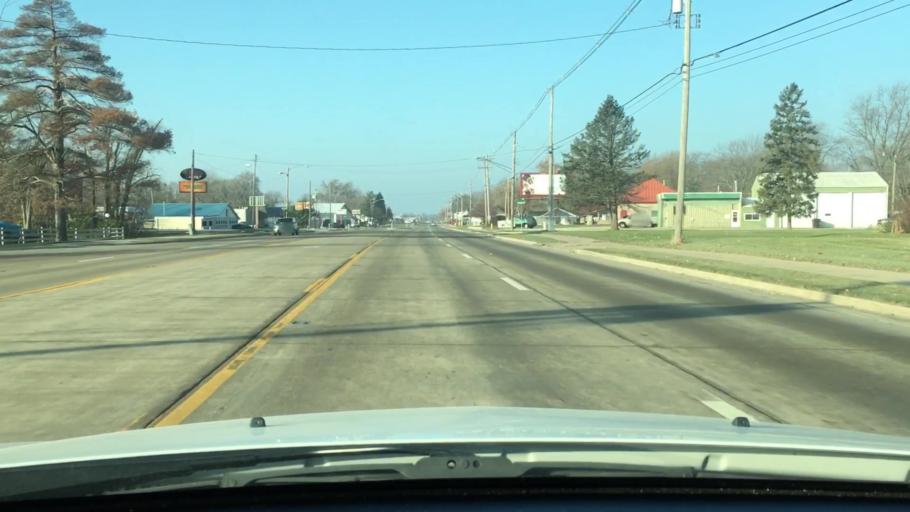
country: US
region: Illinois
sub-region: Woodford County
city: Germantown Hills
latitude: 40.6925
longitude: -89.4871
